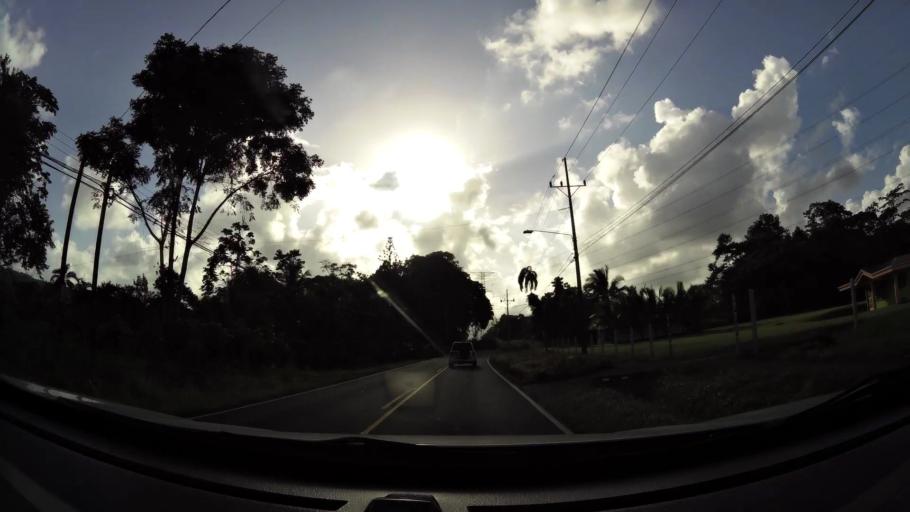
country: CR
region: Limon
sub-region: Canton de Siquirres
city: Siquirres
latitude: 10.0968
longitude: -83.5287
